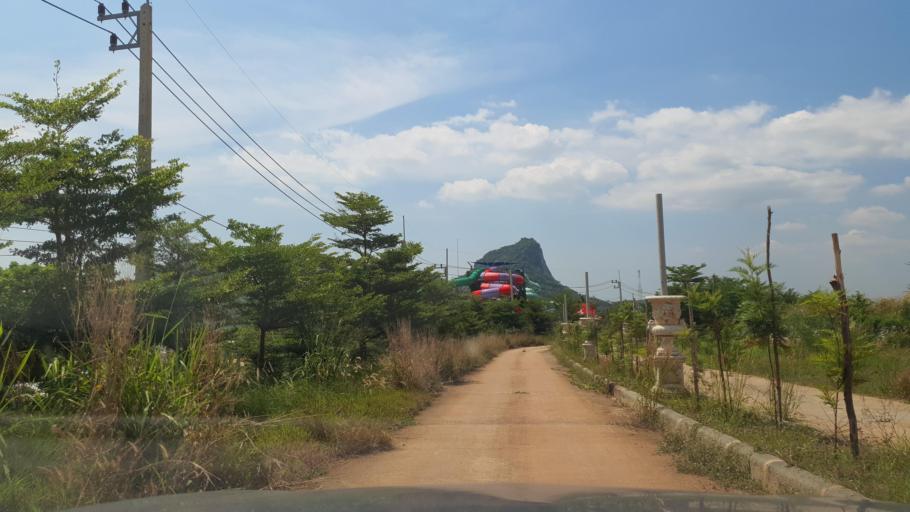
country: TH
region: Rayong
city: Ban Chang
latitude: 12.7516
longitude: 100.9638
